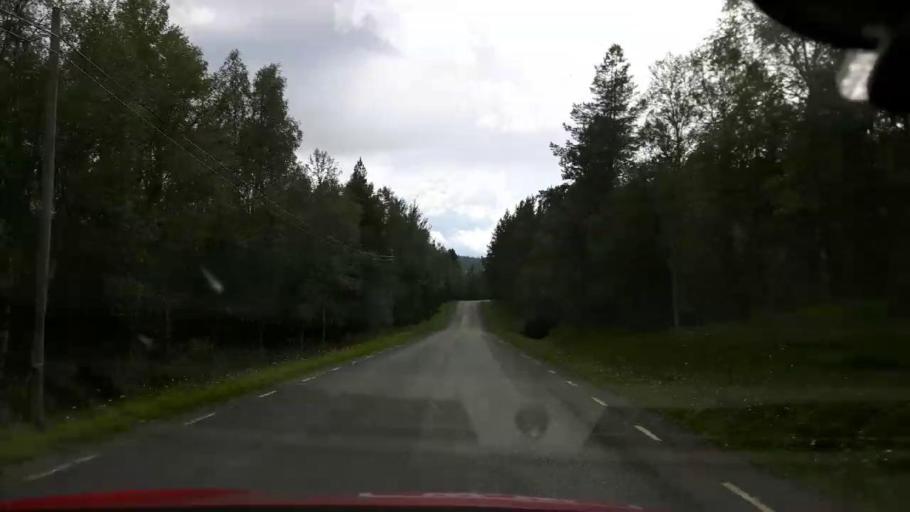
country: SE
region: Jaemtland
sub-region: Are Kommun
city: Are
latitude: 63.1502
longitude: 12.9985
